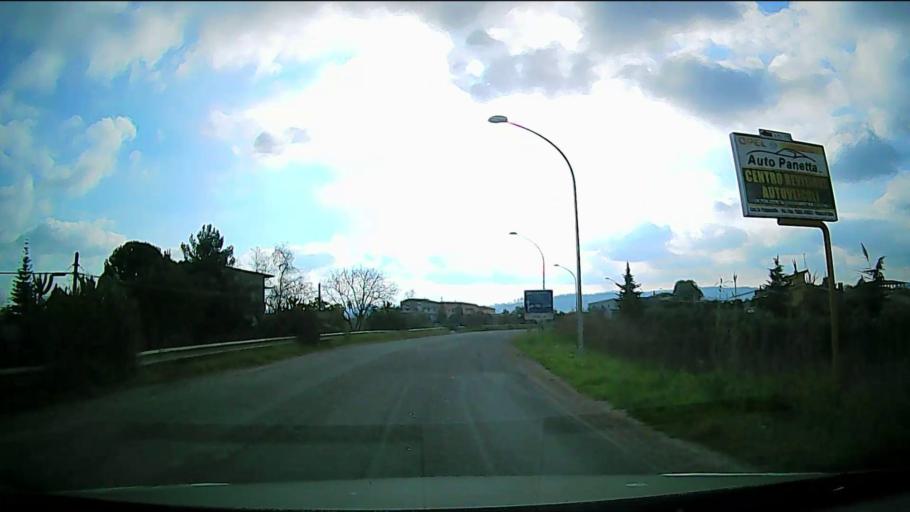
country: IT
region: Calabria
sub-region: Provincia di Crotone
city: Rocca di Neto
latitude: 39.1795
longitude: 17.0171
